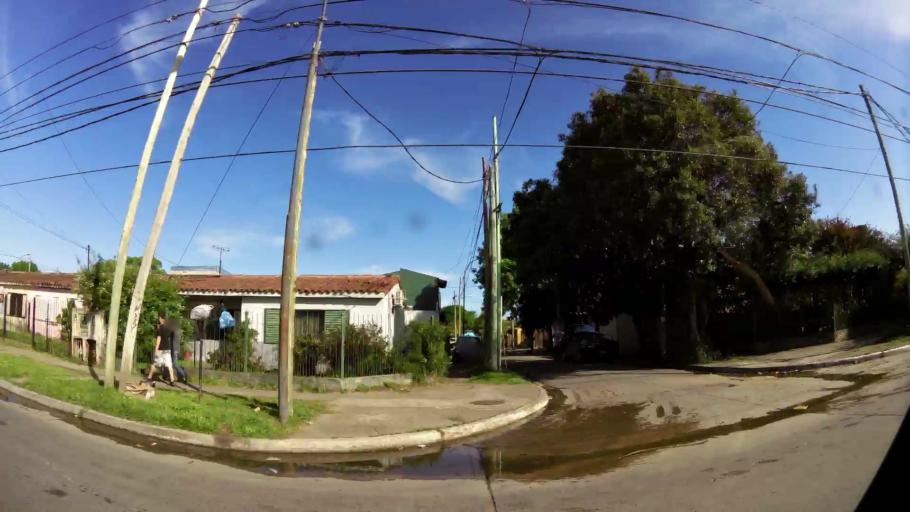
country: AR
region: Buenos Aires
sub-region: Partido de Quilmes
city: Quilmes
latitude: -34.7912
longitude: -58.2293
